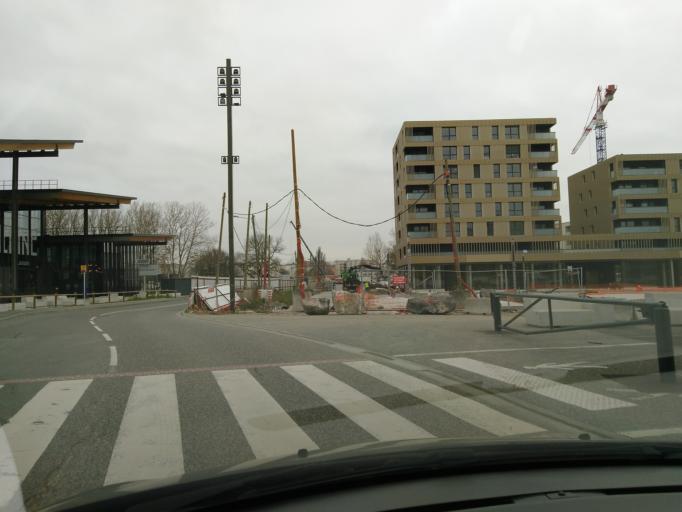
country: FR
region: Midi-Pyrenees
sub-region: Departement de la Haute-Garonne
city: Ramonville-Saint-Agne
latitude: 43.5719
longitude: 1.4782
